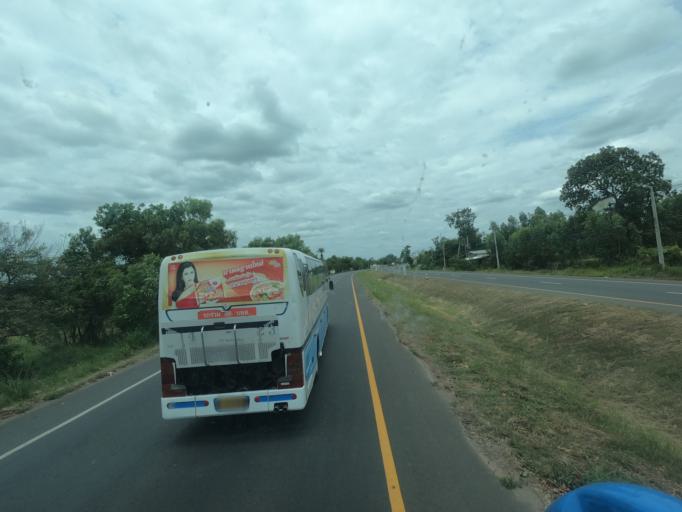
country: TH
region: Buriram
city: Prakhon Chai
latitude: 14.6069
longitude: 103.1256
